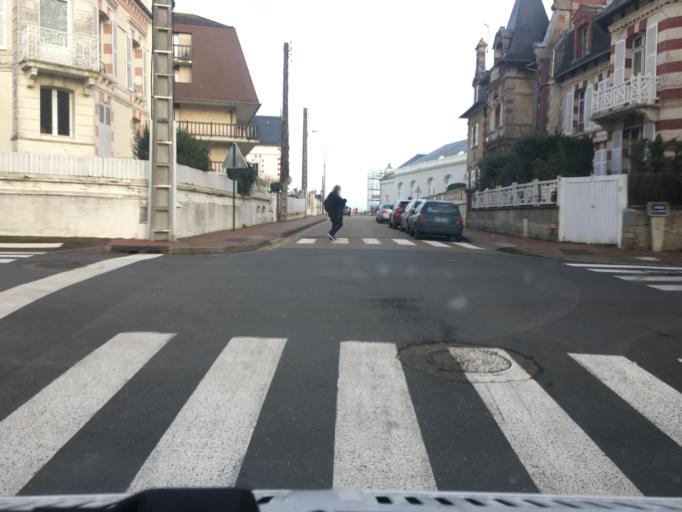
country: FR
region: Lower Normandy
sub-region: Departement du Calvados
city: Cabourg
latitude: 49.2929
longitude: -0.1169
